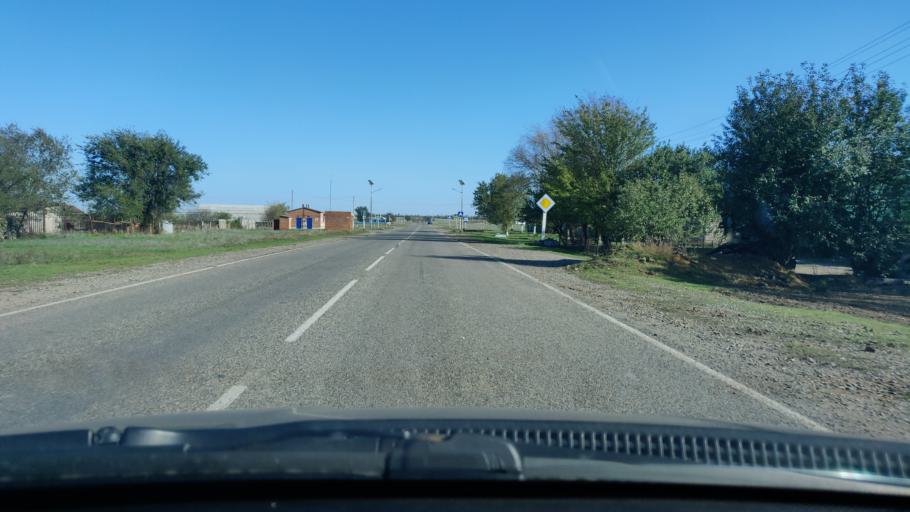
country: RU
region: Stavropol'skiy
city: Letnyaya Stavka
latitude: 45.3751
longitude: 43.6844
